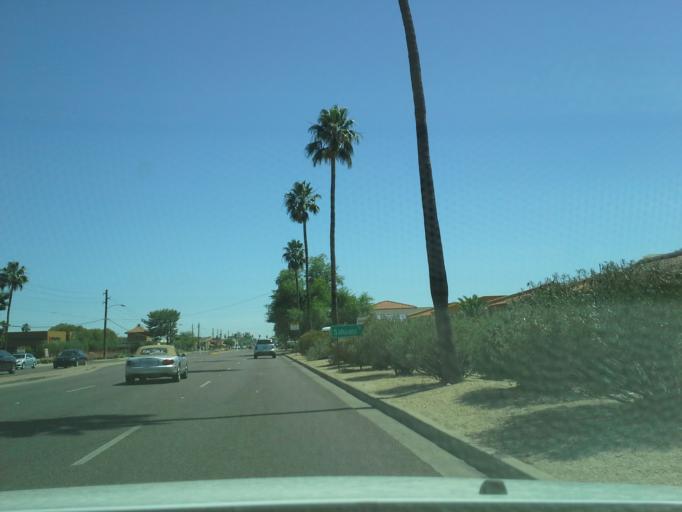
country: US
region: Arizona
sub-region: Maricopa County
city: Paradise Valley
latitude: 33.5852
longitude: -111.9261
